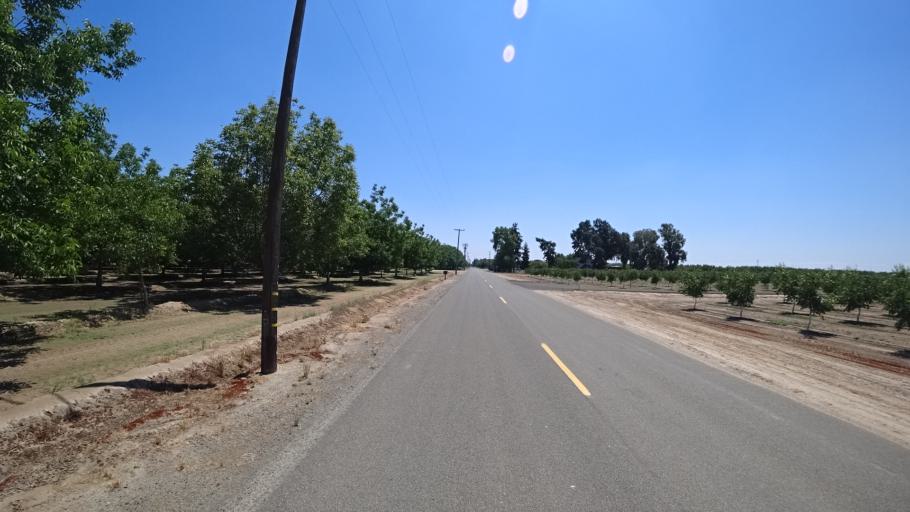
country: US
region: California
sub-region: Kings County
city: Lucerne
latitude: 36.4077
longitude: -119.6549
